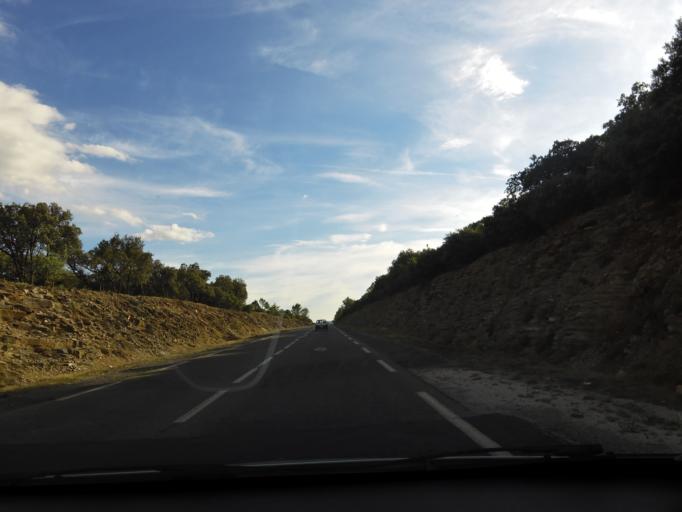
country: FR
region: Languedoc-Roussillon
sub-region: Departement du Gard
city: Quissac
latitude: 43.8803
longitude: 3.9660
